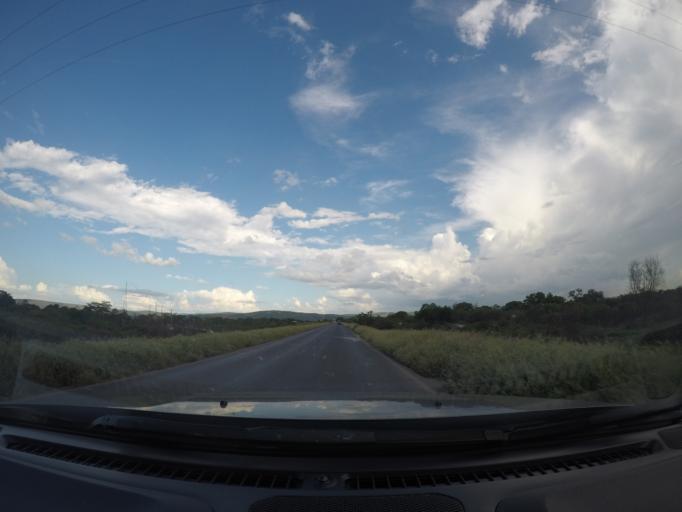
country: BR
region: Bahia
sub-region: Ibotirama
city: Ibotirama
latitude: -12.1808
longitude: -43.2377
